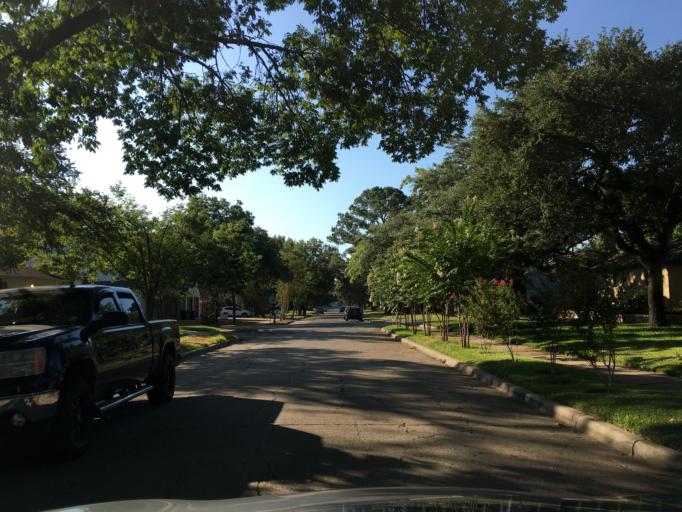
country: US
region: Texas
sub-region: Dallas County
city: Highland Park
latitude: 32.8532
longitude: -96.7108
